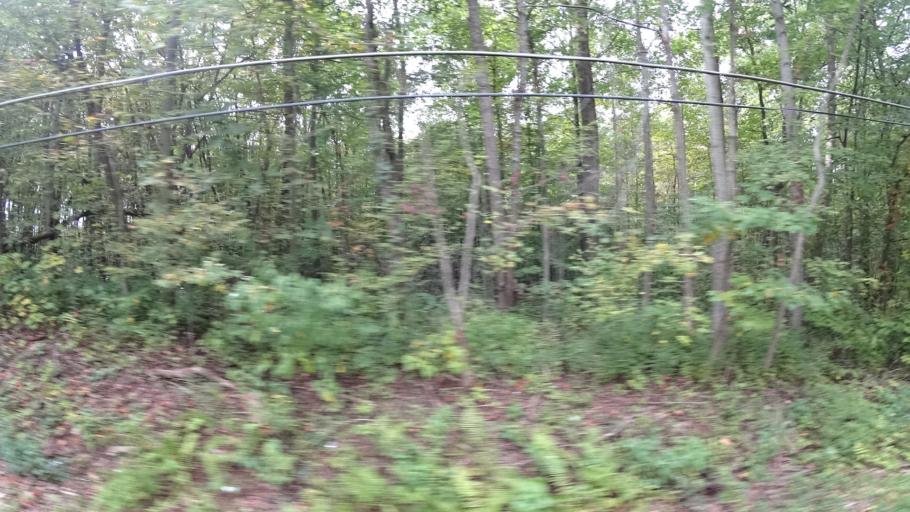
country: US
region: Indiana
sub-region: LaPorte County
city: Trail Creek
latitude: 41.7151
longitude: -86.8163
